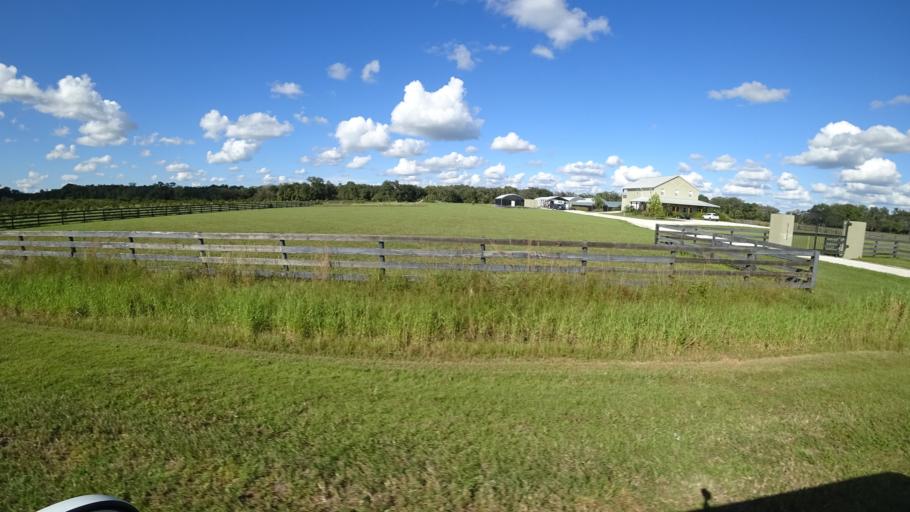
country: US
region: Florida
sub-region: Sarasota County
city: Lake Sarasota
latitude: 27.2889
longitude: -82.2215
